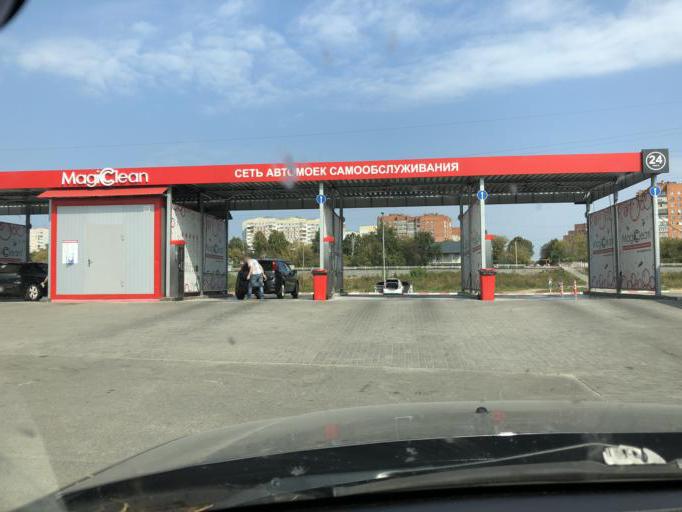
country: RU
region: Tula
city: Tula
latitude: 54.1932
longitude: 37.6429
